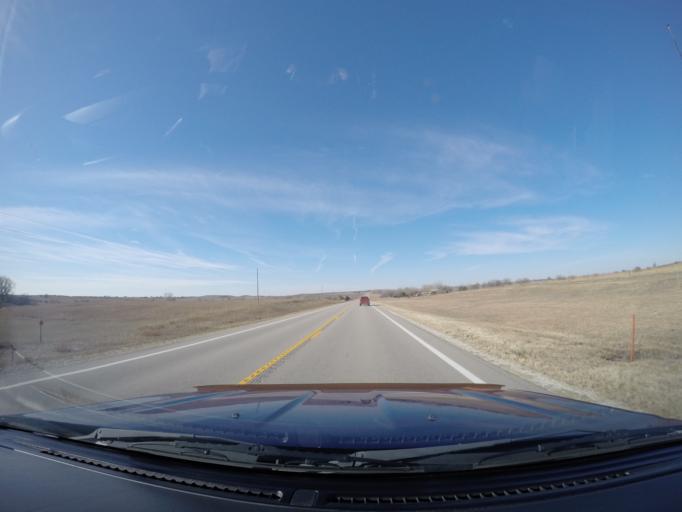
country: US
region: Kansas
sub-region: Clay County
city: Clay Center
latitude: 39.3784
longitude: -97.3648
